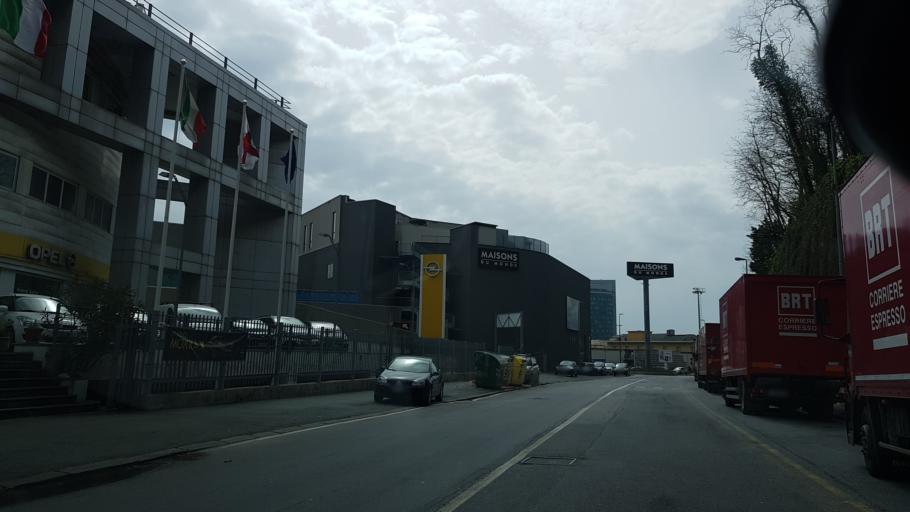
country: IT
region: Liguria
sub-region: Provincia di Genova
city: San Teodoro
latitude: 44.4202
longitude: 8.8785
